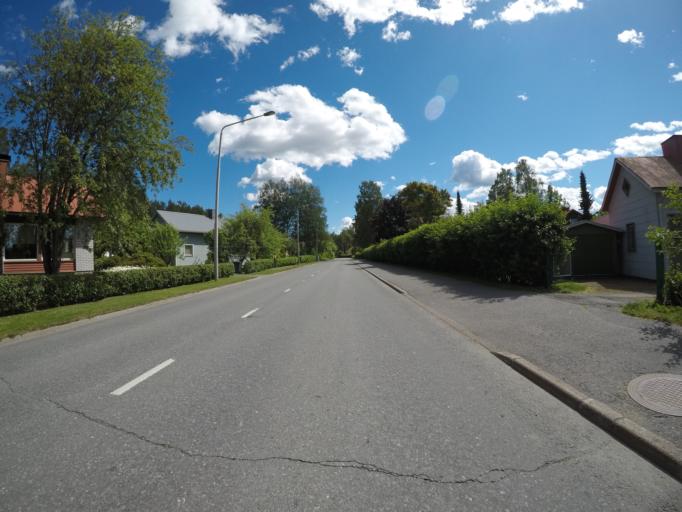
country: FI
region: Haeme
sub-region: Haemeenlinna
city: Haemeenlinna
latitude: 61.0117
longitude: 24.4325
